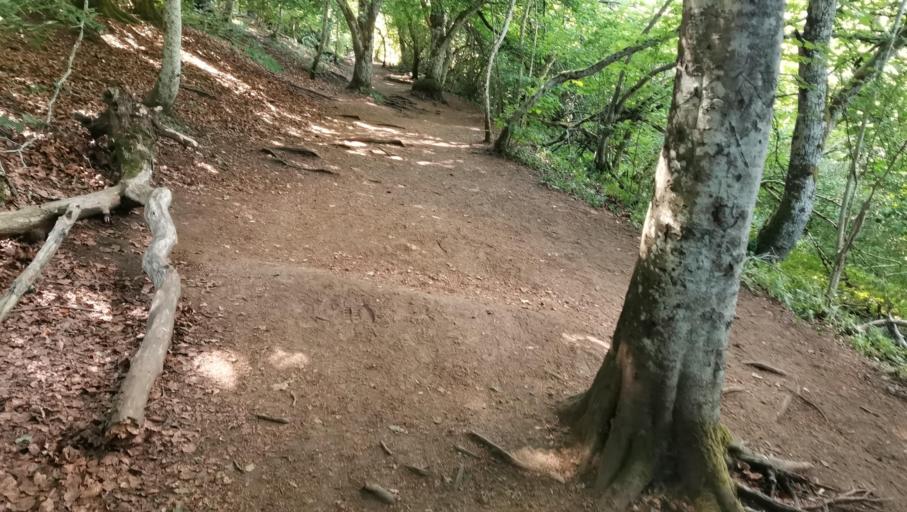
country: FR
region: Auvergne
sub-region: Departement du Puy-de-Dome
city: Orcines
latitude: 45.7986
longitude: 2.9746
